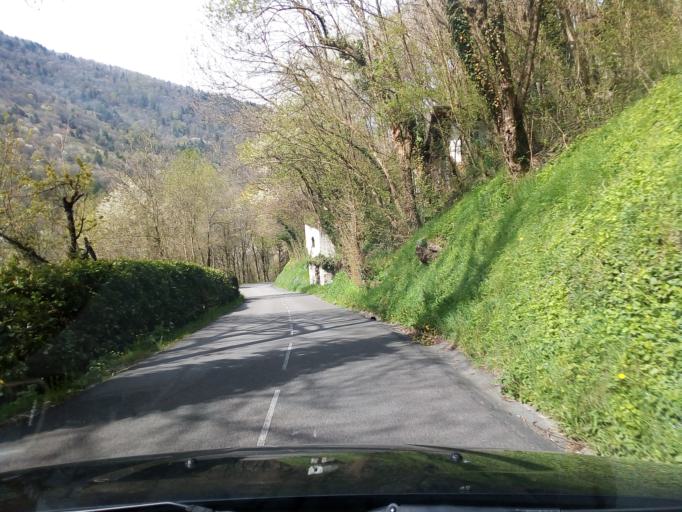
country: FR
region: Rhone-Alpes
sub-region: Departement de l'Isere
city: Gieres
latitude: 45.1630
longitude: 5.8210
